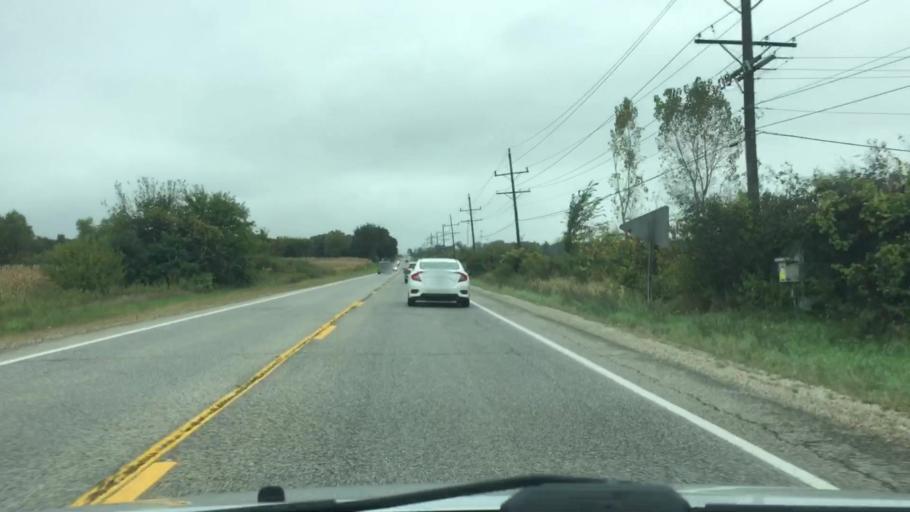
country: US
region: Illinois
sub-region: McHenry County
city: Prairie Grove
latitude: 42.2956
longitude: -88.2871
